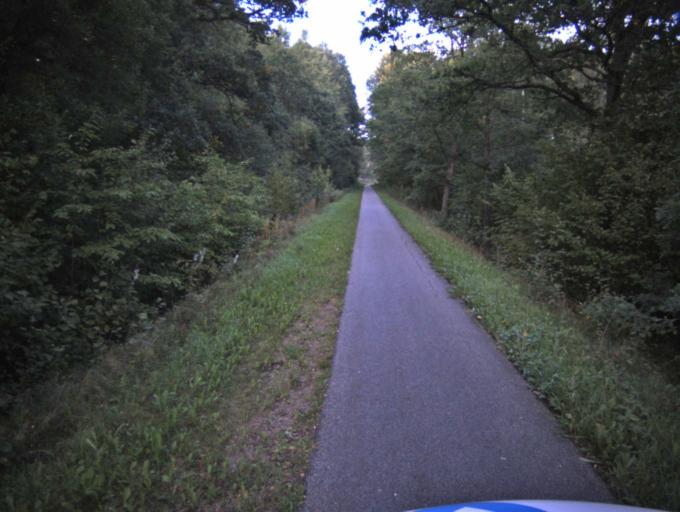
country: SE
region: Vaestra Goetaland
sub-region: Ulricehamns Kommun
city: Ulricehamn
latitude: 57.9095
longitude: 13.4751
